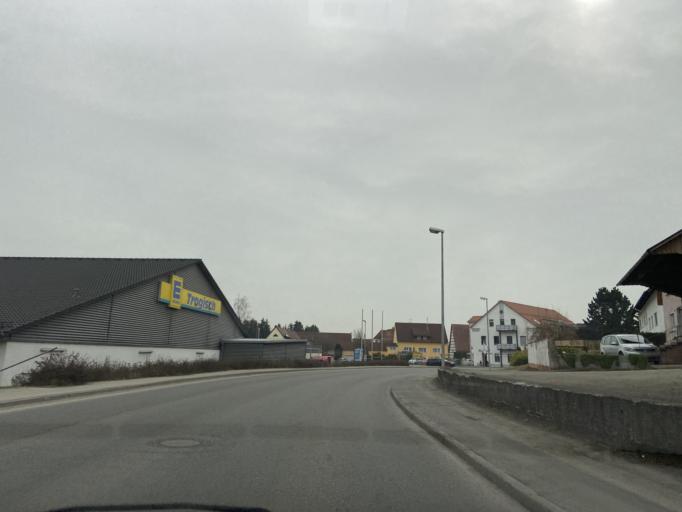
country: DE
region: Baden-Wuerttemberg
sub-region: Tuebingen Region
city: Ostrach
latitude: 47.9560
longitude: 9.3807
